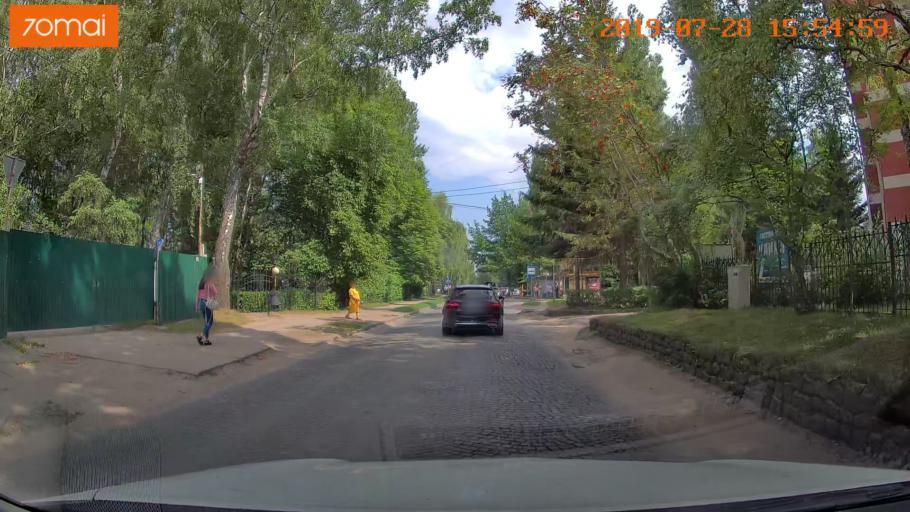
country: RU
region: Kaliningrad
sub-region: Gorod Svetlogorsk
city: Svetlogorsk
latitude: 54.9414
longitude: 20.1375
